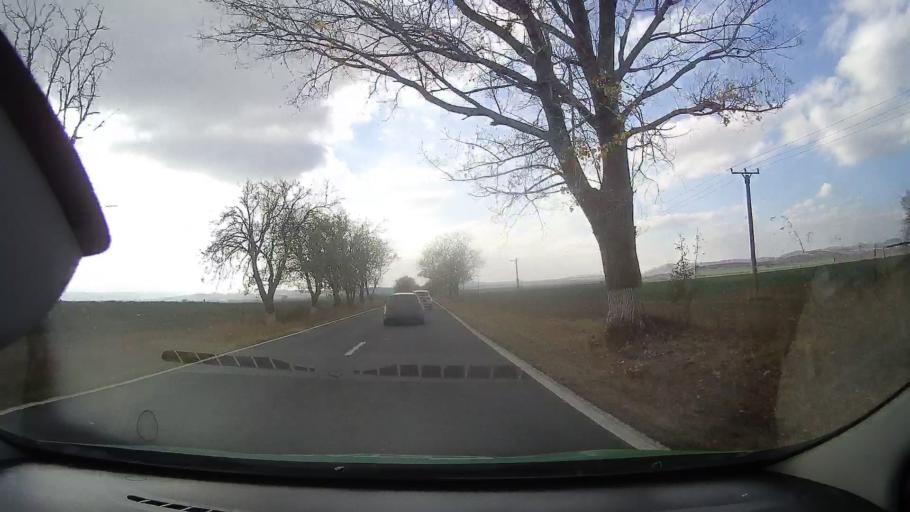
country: RO
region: Tulcea
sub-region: Comuna Frecatei
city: Frecatei
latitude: 45.0702
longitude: 28.6571
